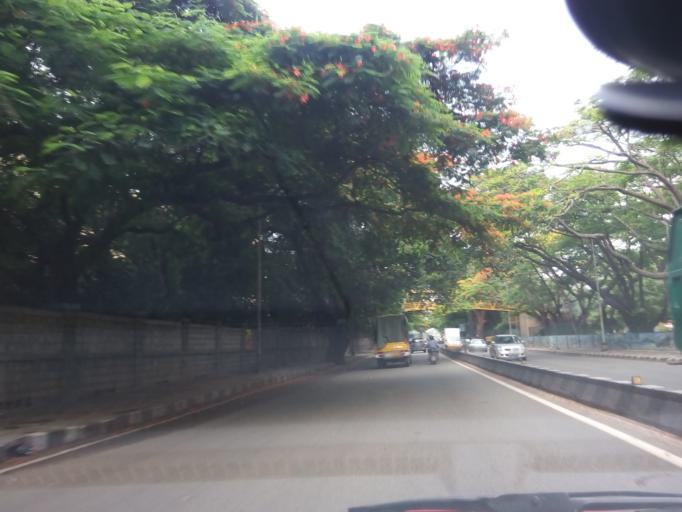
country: IN
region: Karnataka
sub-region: Bangalore Urban
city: Bangalore
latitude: 13.0166
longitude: 77.5617
